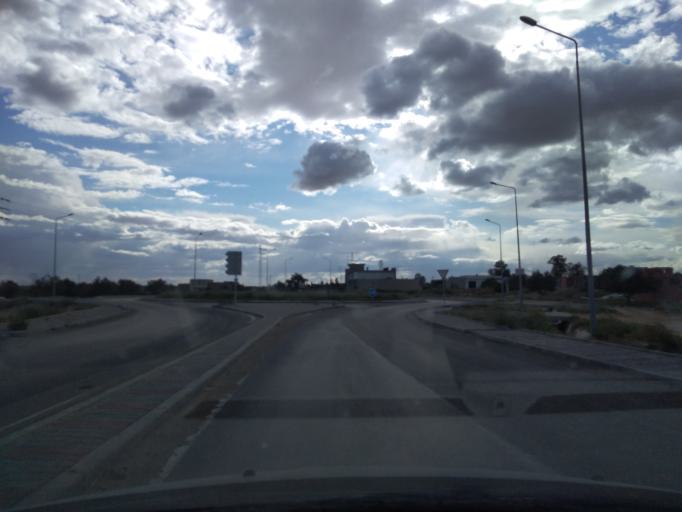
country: TN
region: Susah
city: Masakin
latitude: 35.7111
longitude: 10.5572
